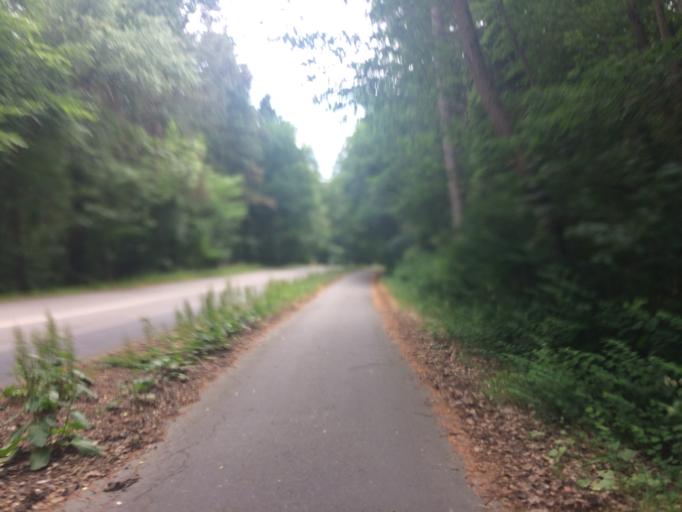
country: DK
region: Capital Region
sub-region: Bornholm Kommune
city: Ronne
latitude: 55.1663
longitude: 14.7147
